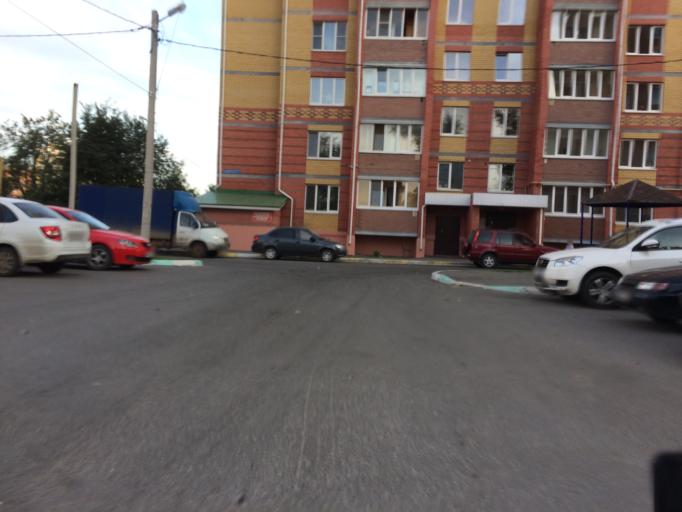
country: RU
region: Mariy-El
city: Yoshkar-Ola
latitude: 56.6294
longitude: 47.8481
